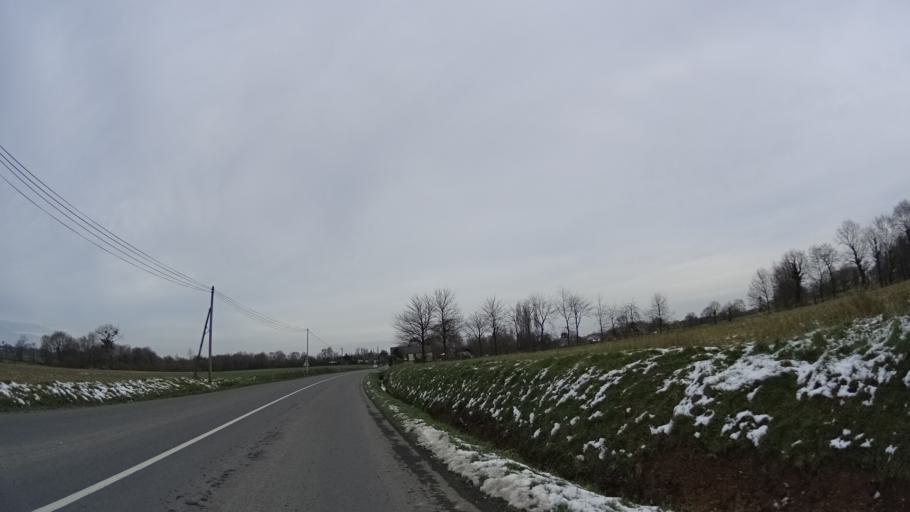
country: FR
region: Brittany
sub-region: Departement d'Ille-et-Vilaine
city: Montauban-de-Bretagne
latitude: 48.2273
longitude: -2.0229
